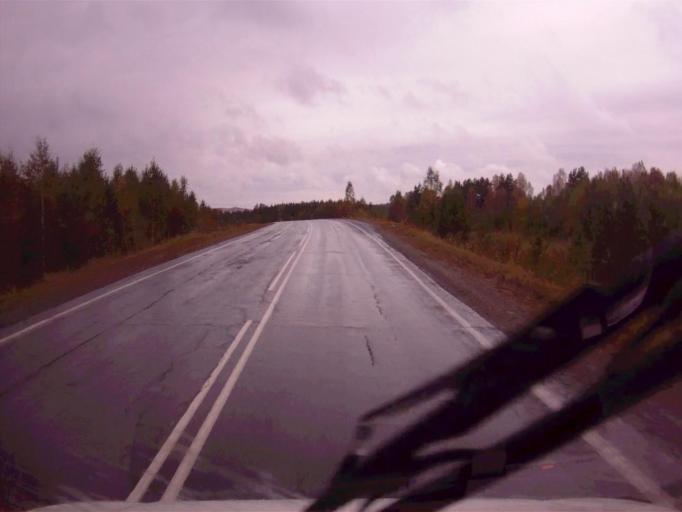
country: RU
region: Chelyabinsk
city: Verkhniy Ufaley
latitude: 56.0075
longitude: 60.3253
